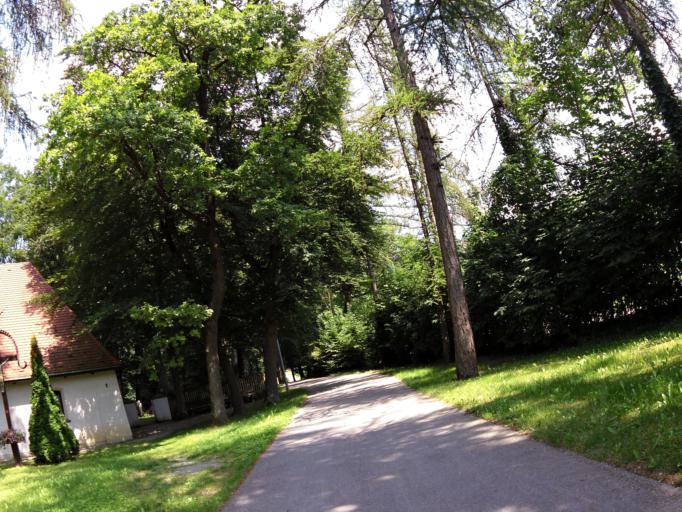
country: DE
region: Bavaria
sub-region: Upper Bavaria
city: Inning am Ammersee
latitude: 48.0574
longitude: 11.1413
